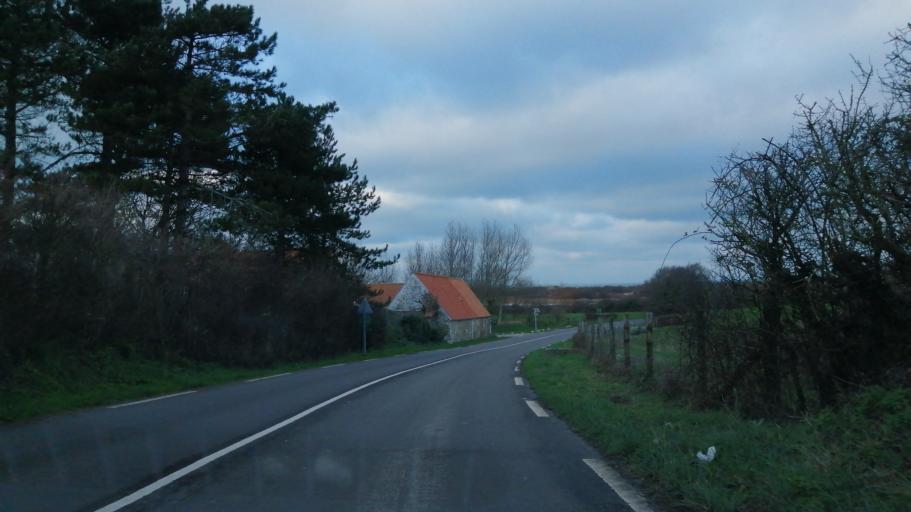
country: FR
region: Nord-Pas-de-Calais
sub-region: Departement du Pas-de-Calais
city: Wissant
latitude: 50.8675
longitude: 1.6315
